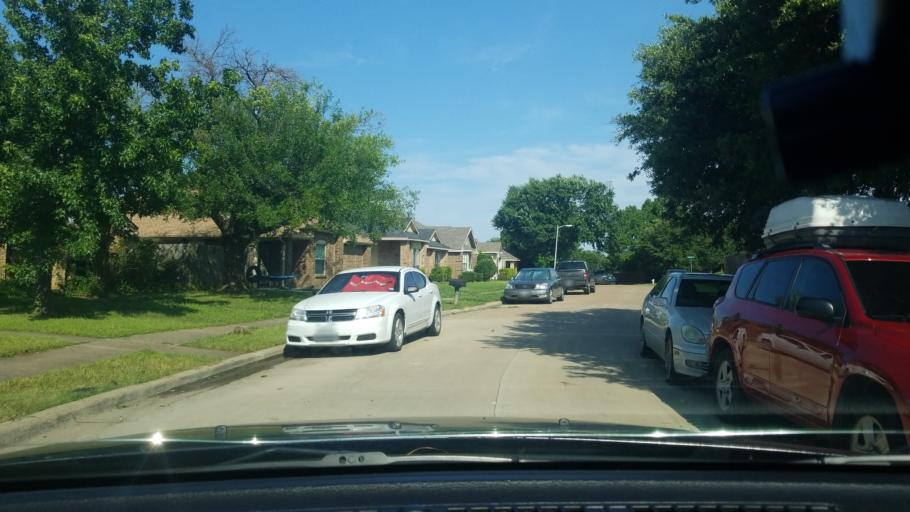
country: US
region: Texas
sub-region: Dallas County
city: Sunnyvale
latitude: 32.7787
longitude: -96.5712
